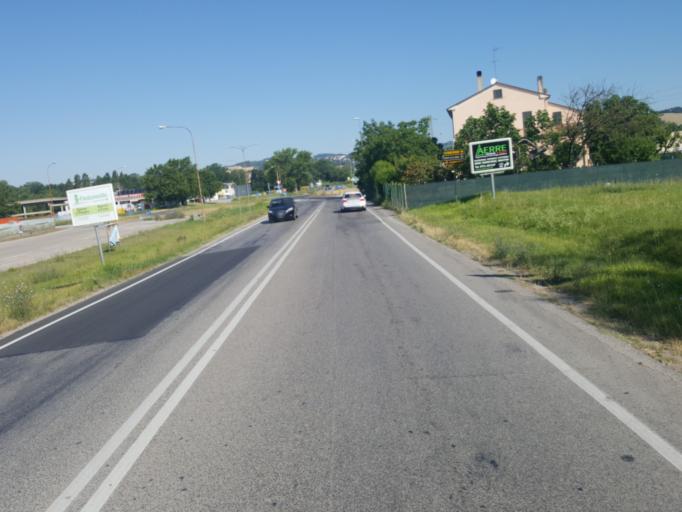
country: IT
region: The Marches
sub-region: Provincia di Pesaro e Urbino
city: Borgo Santa Maria
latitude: 43.8628
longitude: 12.8159
